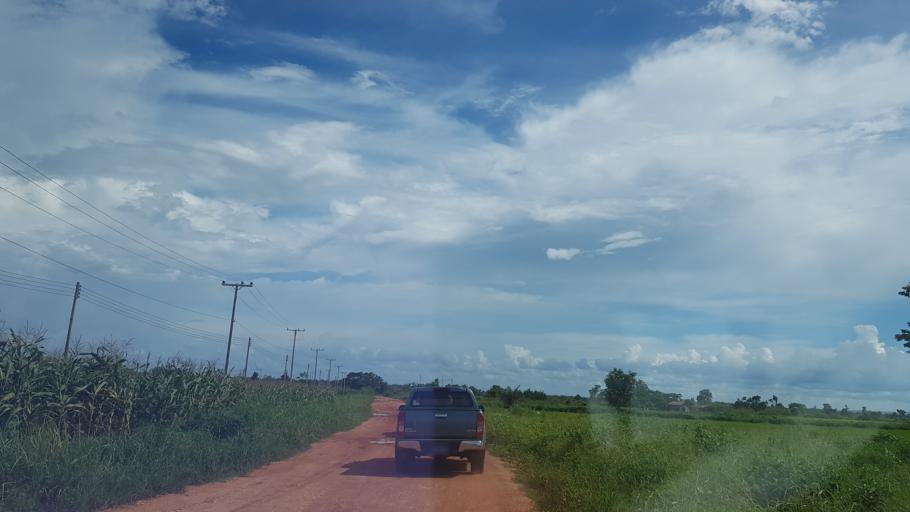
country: LA
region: Vientiane
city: Vientiane
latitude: 18.2126
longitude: 102.5662
